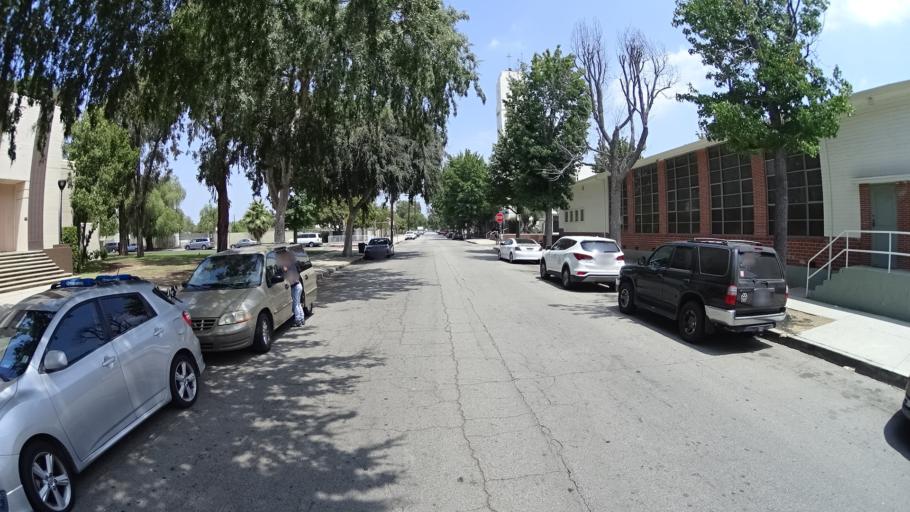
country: US
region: California
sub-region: Los Angeles County
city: Van Nuys
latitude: 34.1902
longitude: -118.4531
